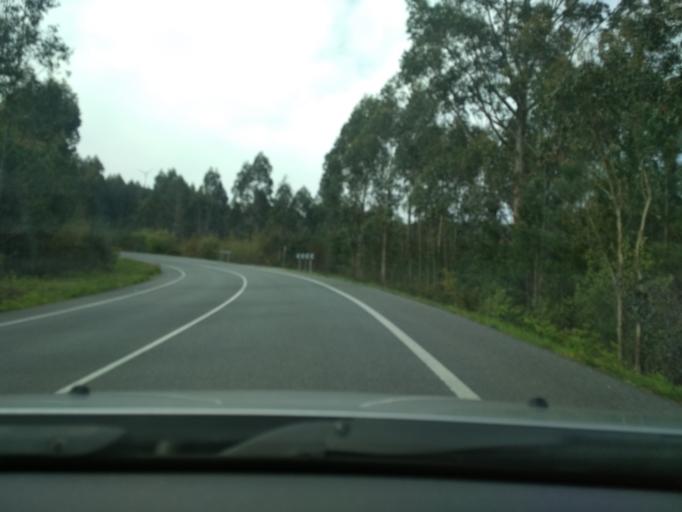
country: ES
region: Galicia
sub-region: Provincia de Pontevedra
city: Catoira
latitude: 42.6598
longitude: -8.7034
